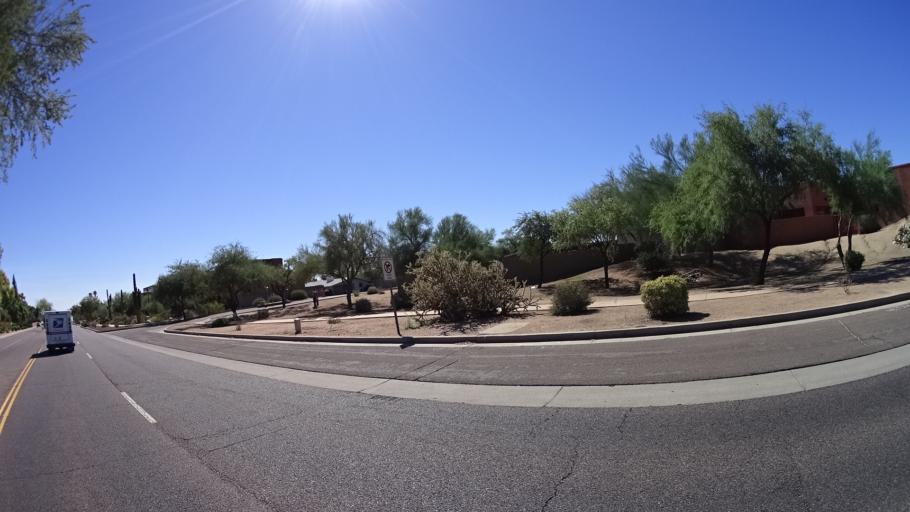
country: US
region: Arizona
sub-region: Maricopa County
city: Paradise Valley
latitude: 33.5311
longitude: -111.9408
